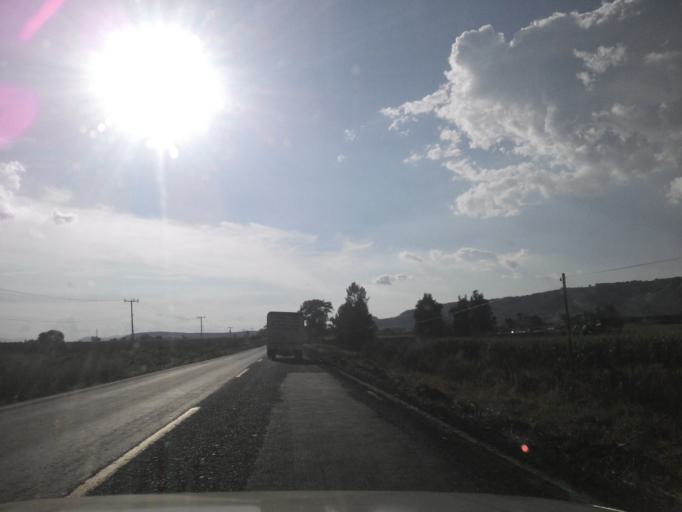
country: MX
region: Jalisco
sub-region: Atotonilco el Alto
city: San Francisco de Asis
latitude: 20.5430
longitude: -102.5994
